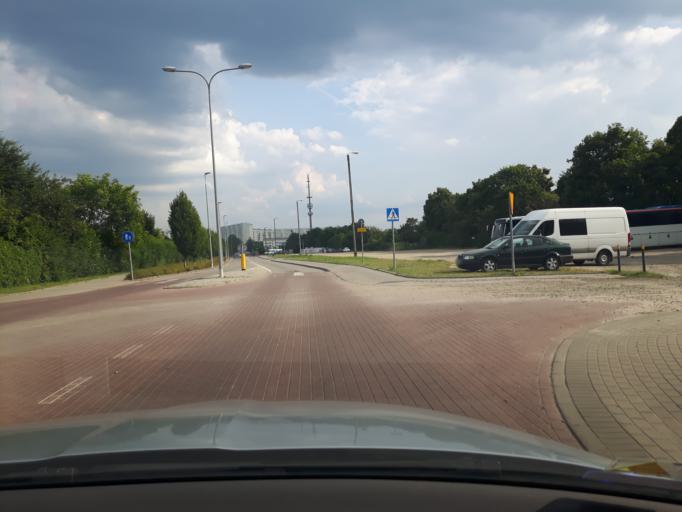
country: PL
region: Pomeranian Voivodeship
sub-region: Sopot
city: Sopot
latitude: 54.4292
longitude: 18.5743
